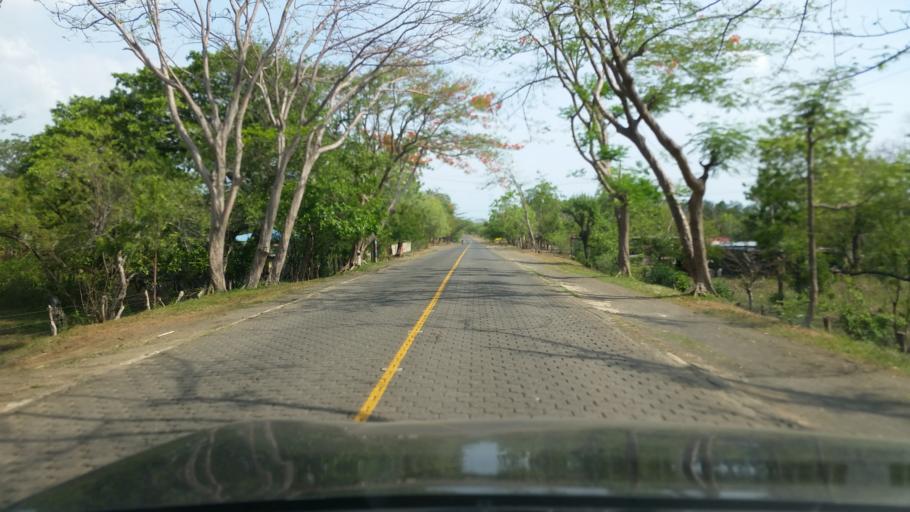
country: NI
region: Managua
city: Carlos Fonseca Amador
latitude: 12.0208
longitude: -86.5166
